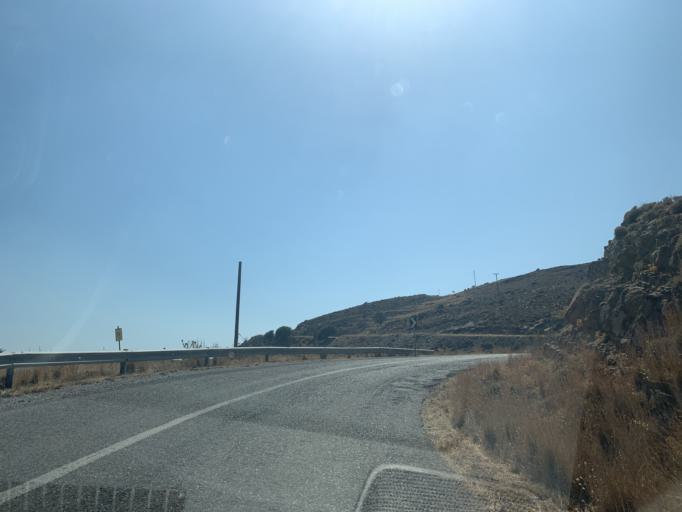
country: GR
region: North Aegean
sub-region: Chios
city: Vrontados
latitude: 38.4806
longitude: 25.8961
